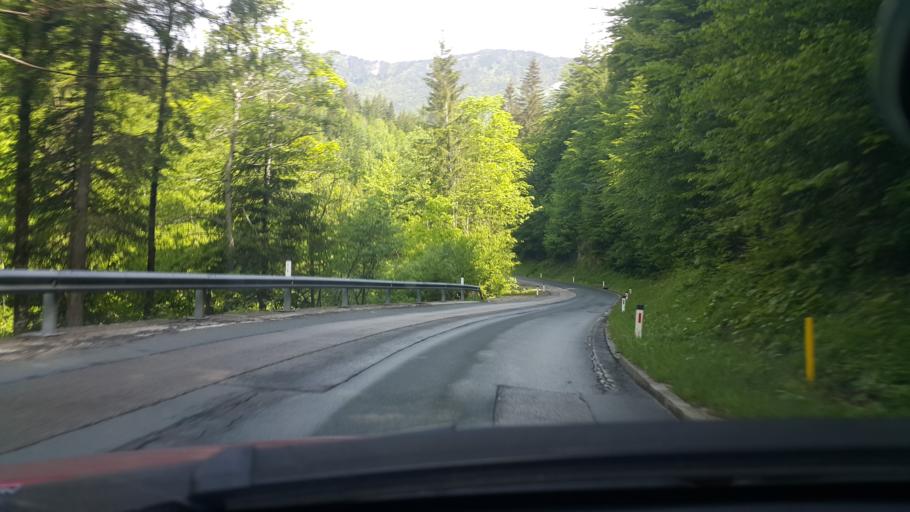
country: AT
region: Carinthia
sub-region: Politischer Bezirk Klagenfurt Land
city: Ferlach
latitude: 46.4687
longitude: 14.2583
